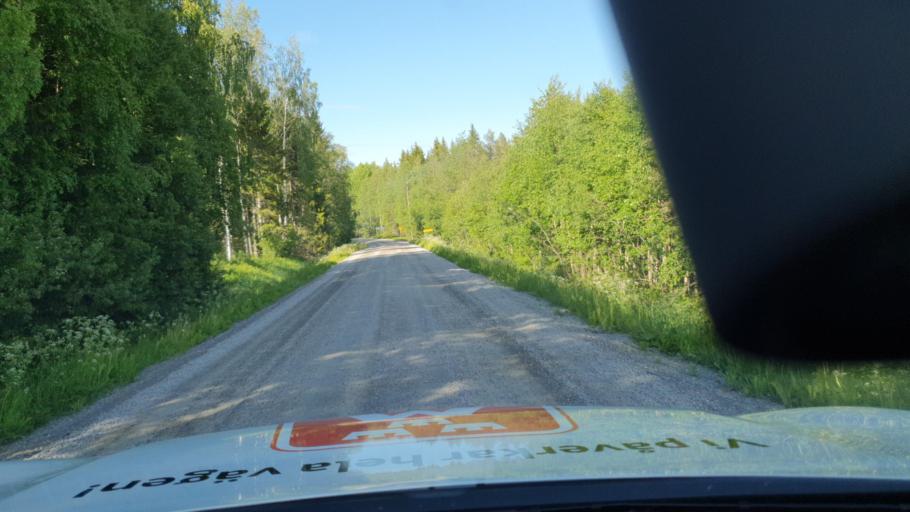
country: SE
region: Vaesterbotten
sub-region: Vannas Kommun
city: Vaennaes
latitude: 63.8033
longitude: 19.6374
